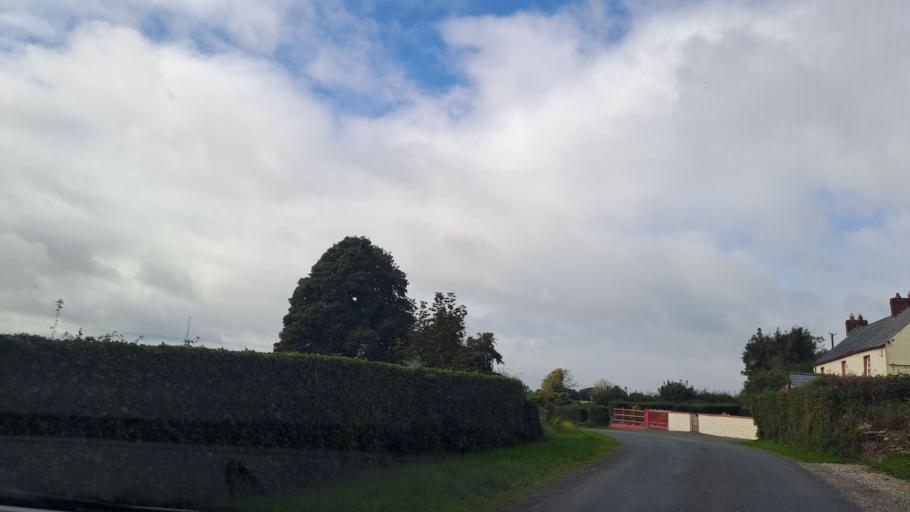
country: IE
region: Ulster
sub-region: An Cabhan
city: Bailieborough
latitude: 53.9720
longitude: -6.8834
